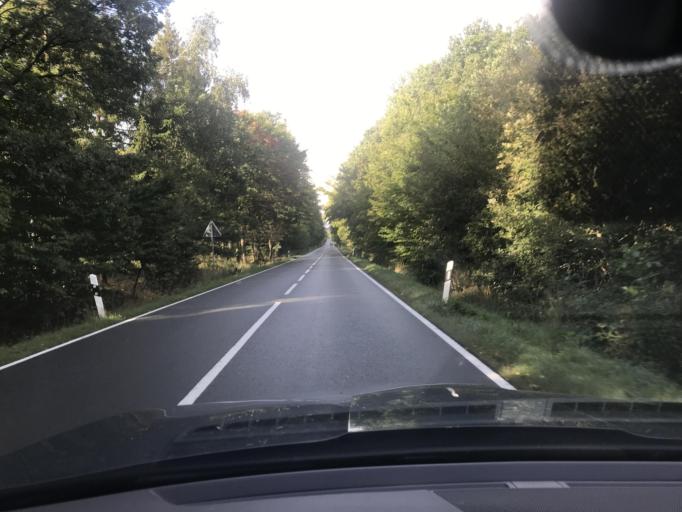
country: DE
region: Saxony-Anhalt
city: Harzgerode
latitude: 51.6007
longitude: 11.0843
